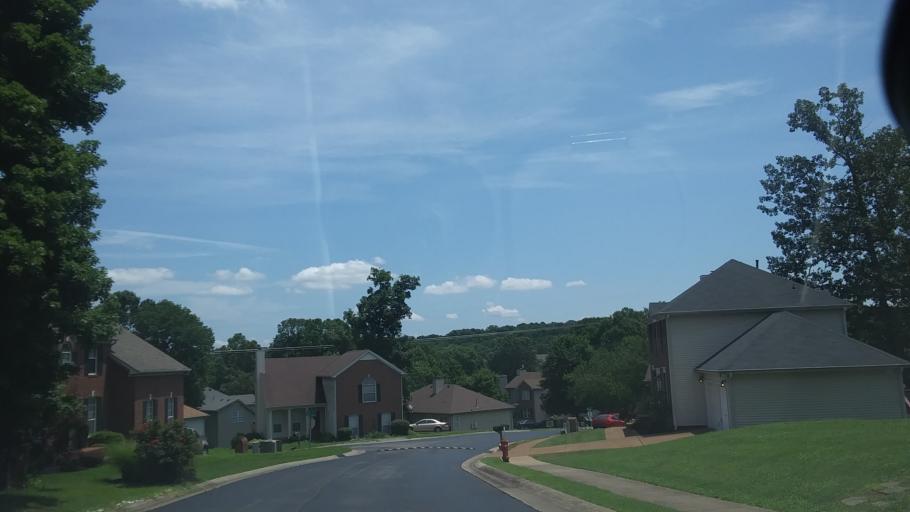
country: US
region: Tennessee
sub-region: Rutherford County
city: La Vergne
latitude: 36.0678
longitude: -86.6278
